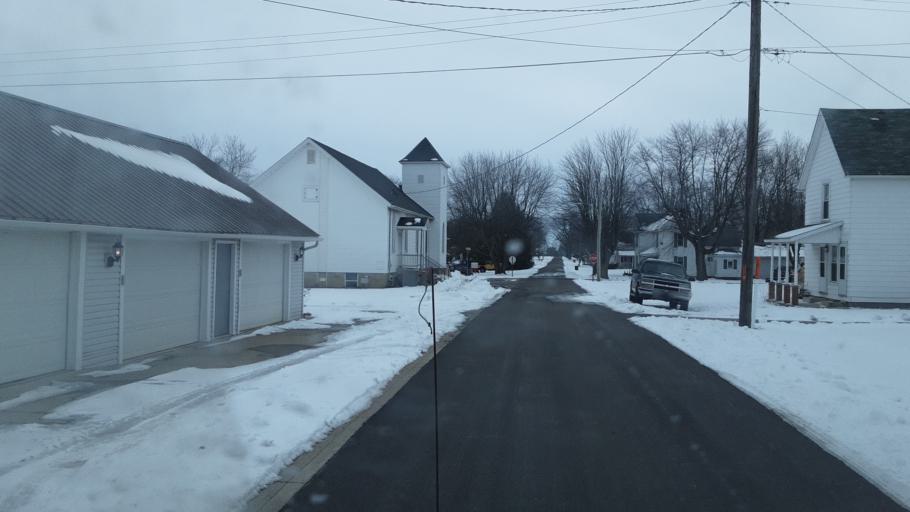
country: US
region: Ohio
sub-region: Madison County
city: Bethel
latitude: 39.7324
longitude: -83.4766
